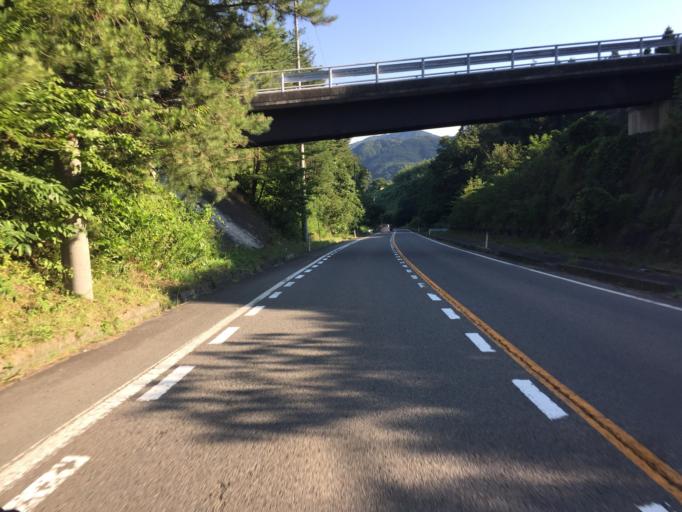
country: JP
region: Miyagi
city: Shiroishi
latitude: 37.9499
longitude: 140.5385
